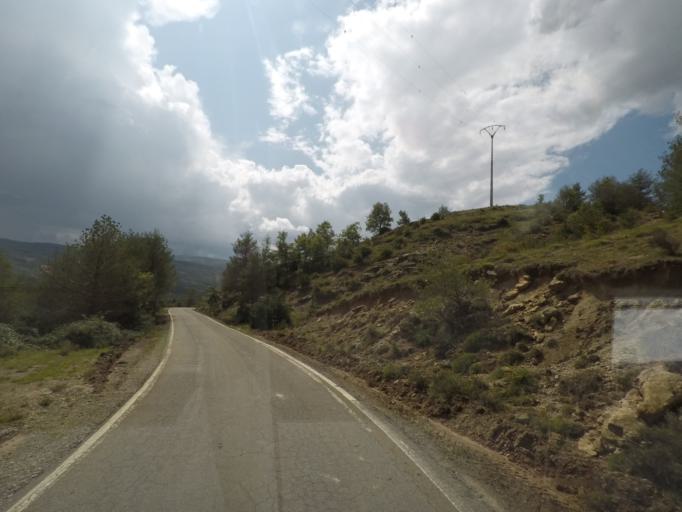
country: ES
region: Aragon
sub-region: Provincia de Huesca
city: Fiscal
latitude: 42.4132
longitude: -0.1270
